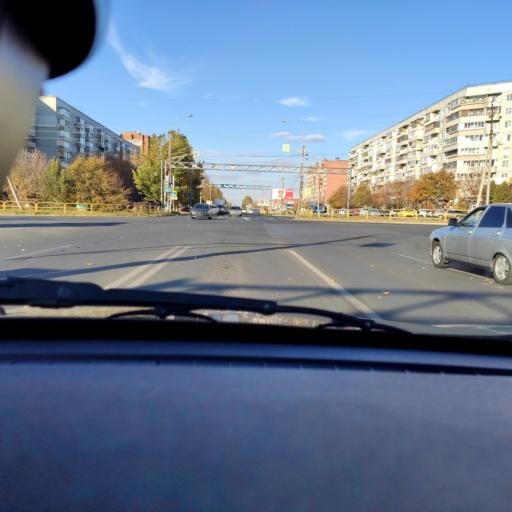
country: RU
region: Samara
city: Tol'yatti
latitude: 53.5408
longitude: 49.3453
